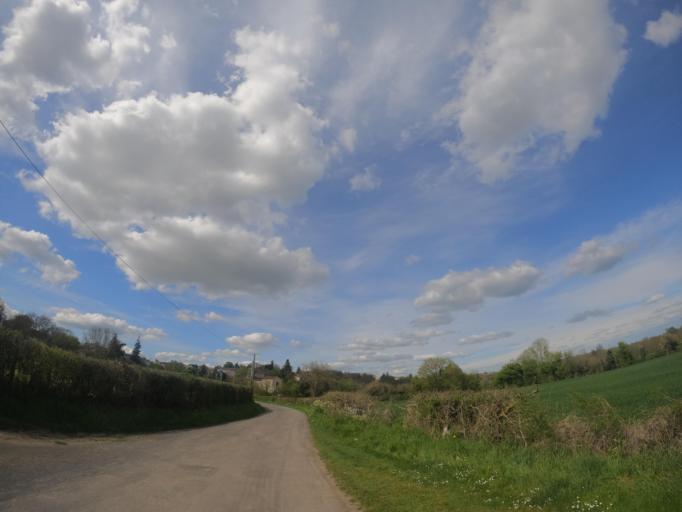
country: FR
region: Poitou-Charentes
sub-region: Departement des Deux-Sevres
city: Saint-Jean-de-Thouars
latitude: 46.9213
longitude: -0.1925
